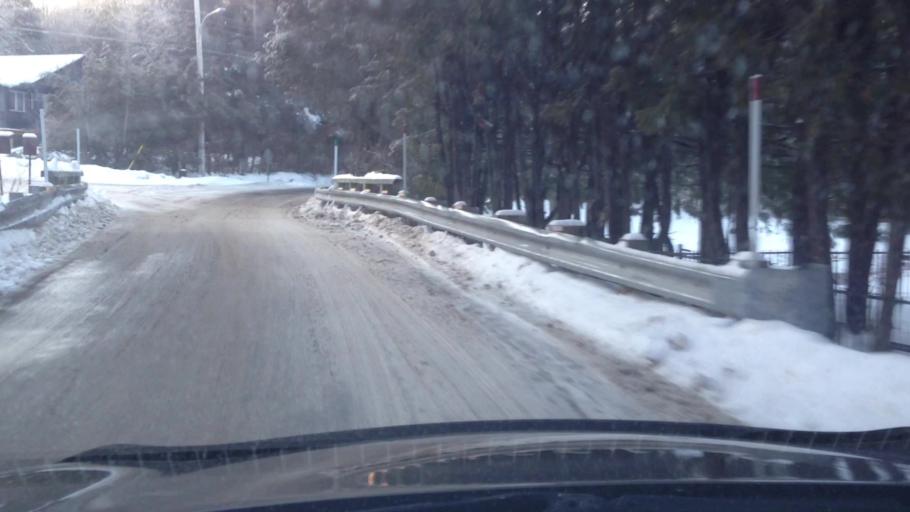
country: CA
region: Quebec
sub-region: Lanaudiere
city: Sainte-Julienne
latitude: 45.9465
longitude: -73.7448
